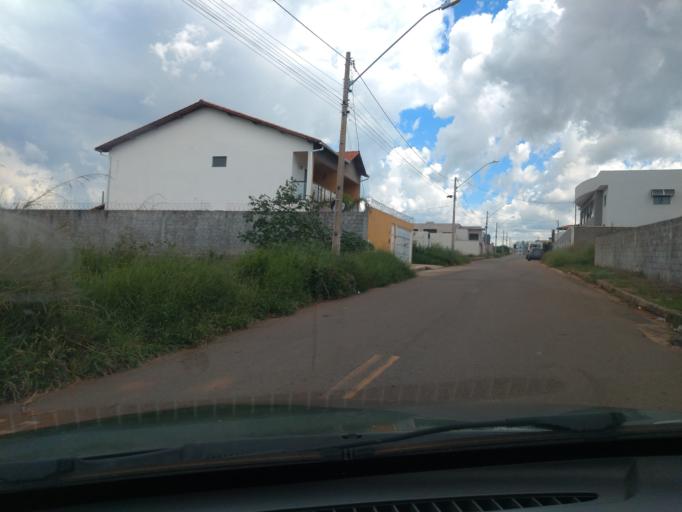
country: BR
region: Minas Gerais
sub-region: Tres Coracoes
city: Tres Coracoes
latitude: -21.6775
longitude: -45.2668
